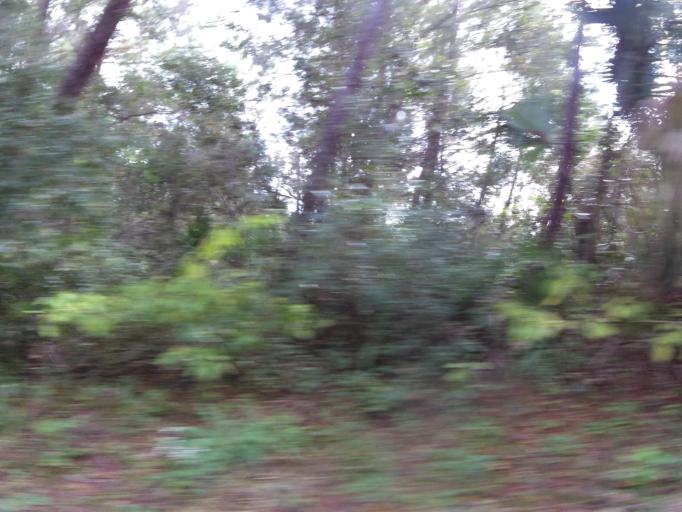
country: US
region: Florida
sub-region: Saint Johns County
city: Villano Beach
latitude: 29.9803
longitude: -81.3886
